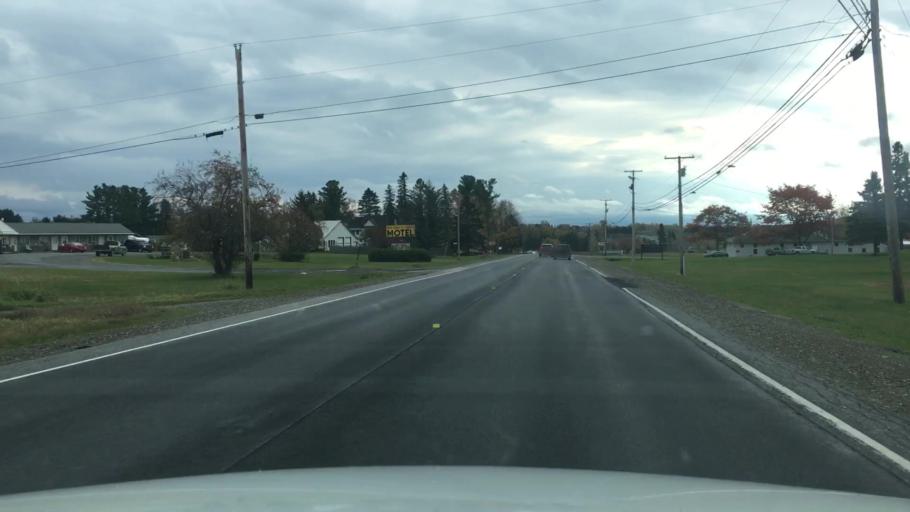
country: US
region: Maine
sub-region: Aroostook County
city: Presque Isle
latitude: 46.6554
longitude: -68.0056
